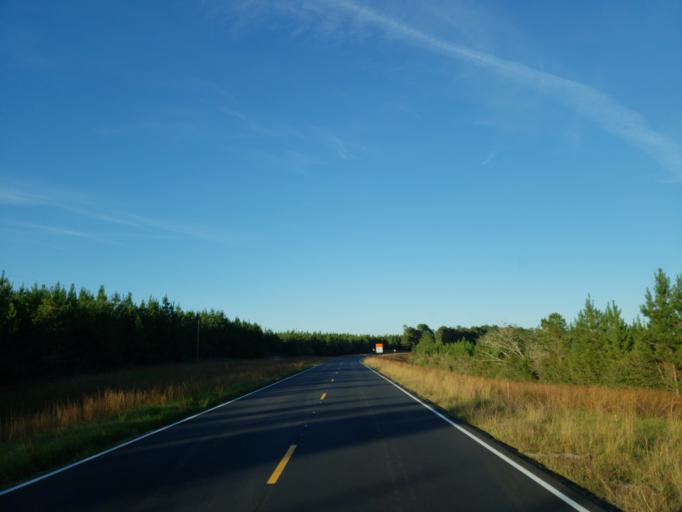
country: US
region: Mississippi
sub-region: Wayne County
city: Belmont
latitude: 31.4210
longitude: -88.5735
